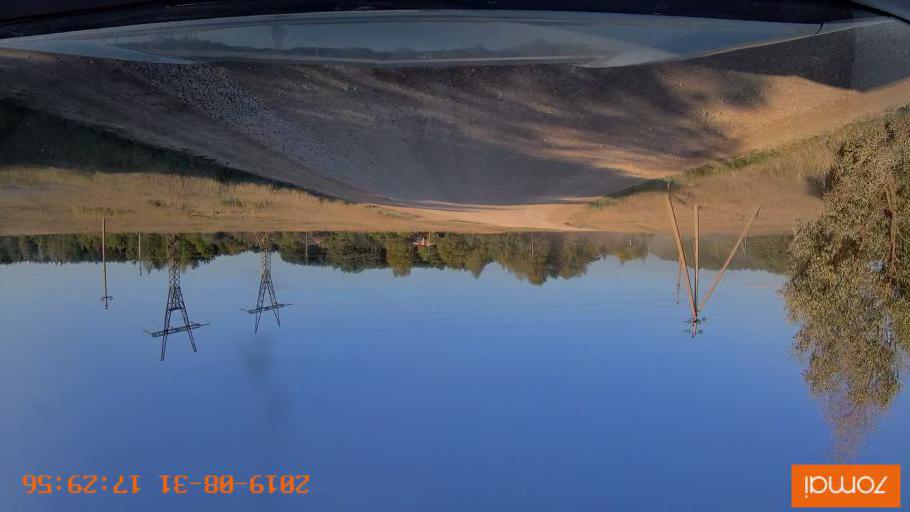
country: RU
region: Kaluga
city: Detchino
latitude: 54.8114
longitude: 36.3295
